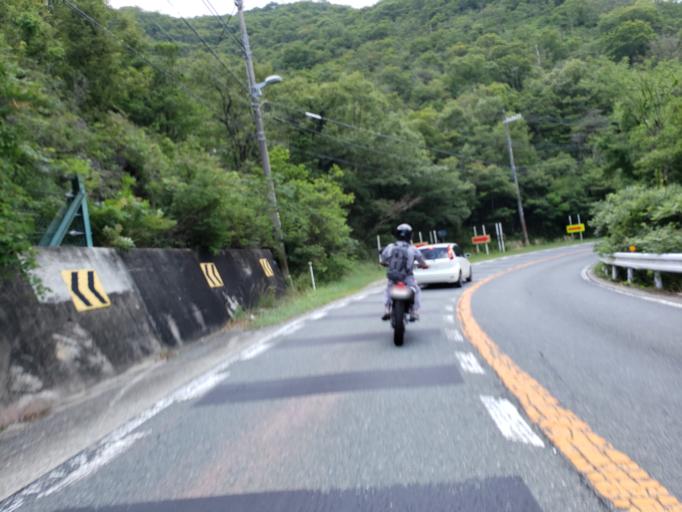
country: JP
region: Hyogo
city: Aioi
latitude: 34.7845
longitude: 134.4393
